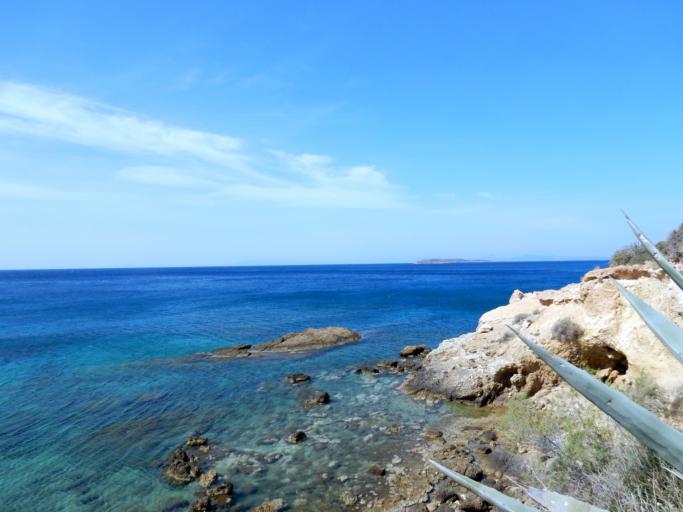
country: GR
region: Attica
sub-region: Nomarchia Anatolikis Attikis
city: Agios Dimitrios Kropias
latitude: 37.8033
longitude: 23.8566
